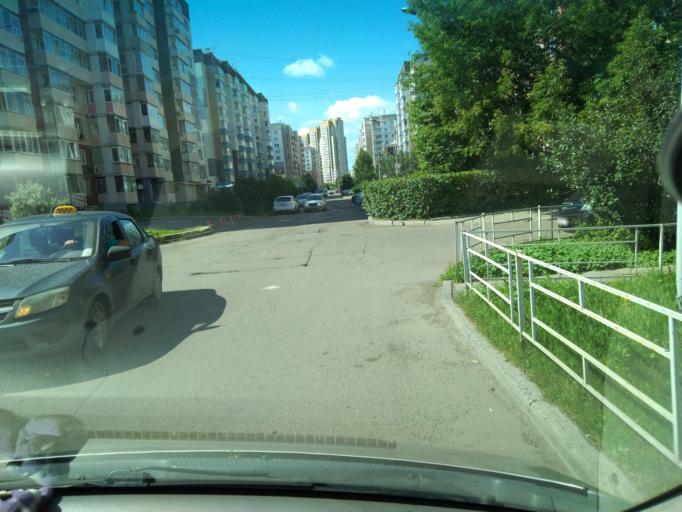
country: RU
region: Krasnoyarskiy
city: Krasnoyarsk
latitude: 56.0437
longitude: 92.9016
